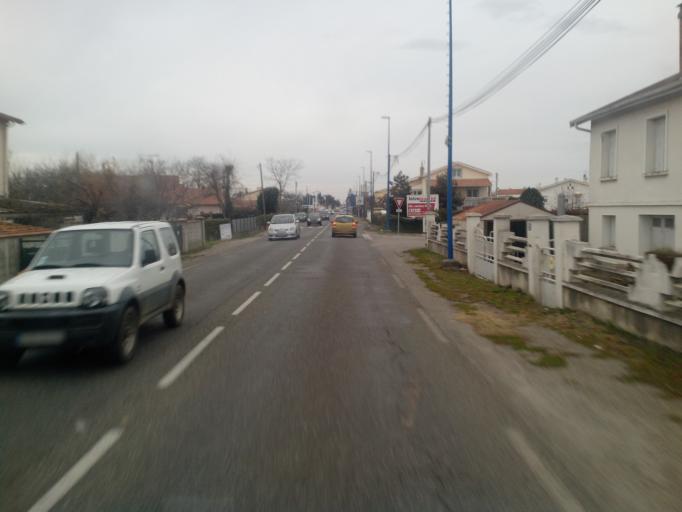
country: FR
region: Midi-Pyrenees
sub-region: Departement de l'Ariege
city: Saint-Jean-du-Falga
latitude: 43.0922
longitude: 1.6264
